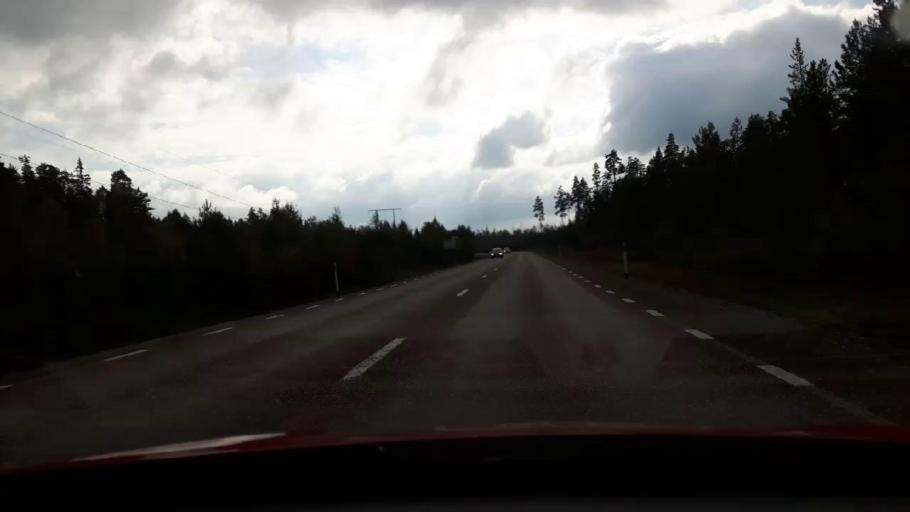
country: SE
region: Gaevleborg
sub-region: Soderhamns Kommun
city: Ljusne
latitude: 61.0936
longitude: 16.9547
